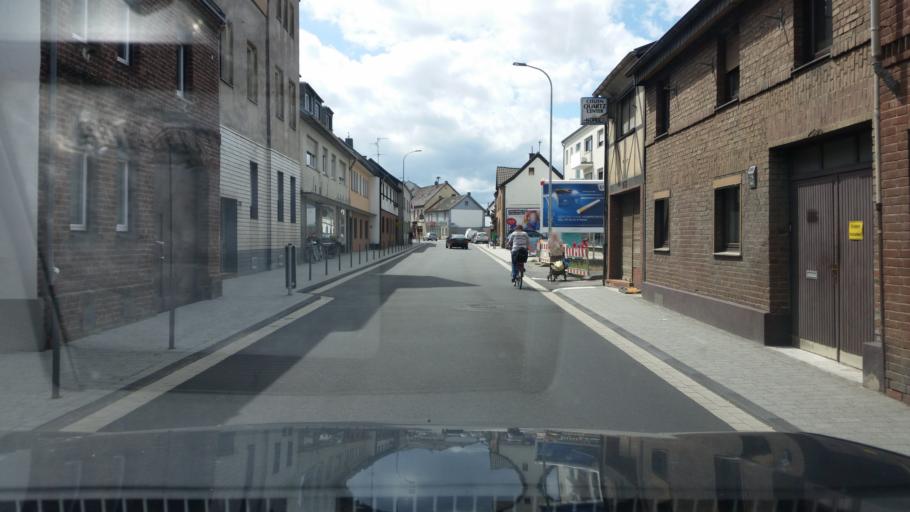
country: DE
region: North Rhine-Westphalia
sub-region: Regierungsbezirk Koln
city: Weilerswist
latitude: 50.7571
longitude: 6.8403
